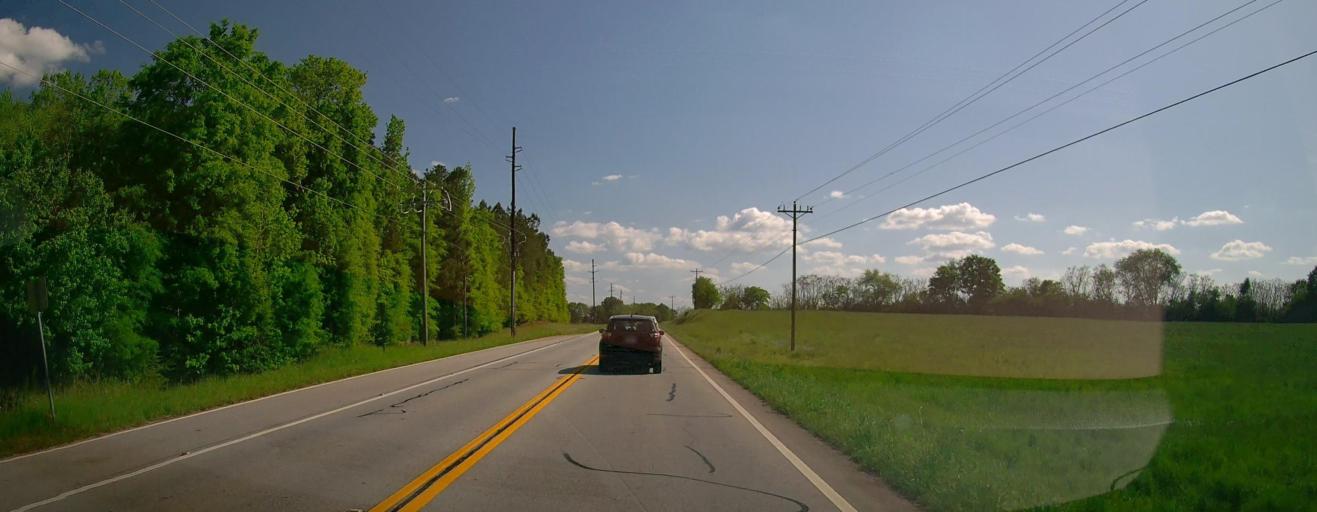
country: US
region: Georgia
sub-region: Morgan County
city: Madison
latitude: 33.5725
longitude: -83.4932
